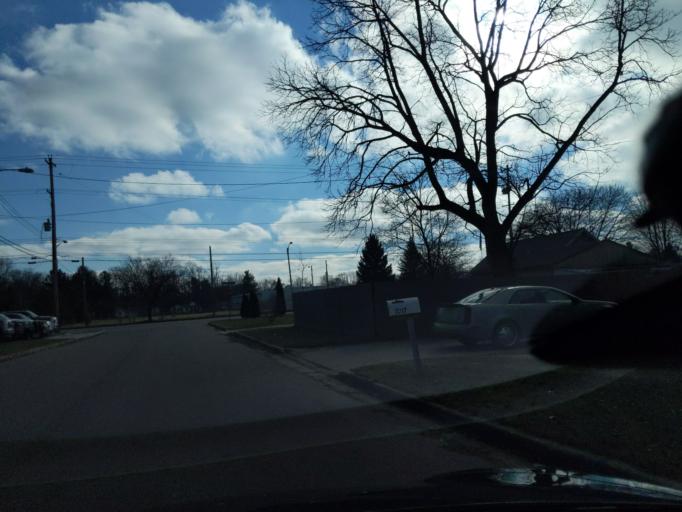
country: US
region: Michigan
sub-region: Ingham County
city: Lansing
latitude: 42.6725
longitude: -84.5805
